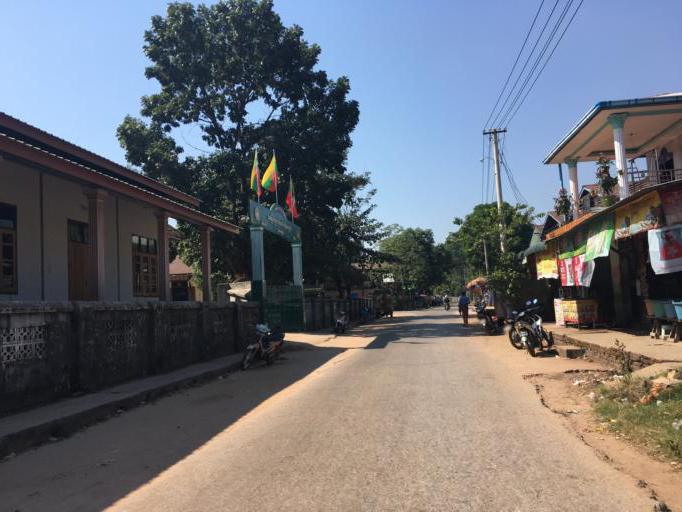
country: MM
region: Mon
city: Mawlamyine
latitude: 16.4349
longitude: 97.7030
